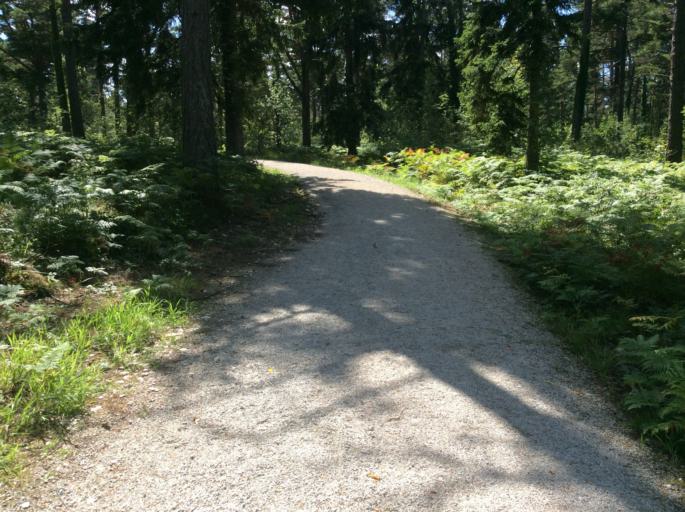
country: SE
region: Gotland
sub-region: Gotland
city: Vibble
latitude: 57.6028
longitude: 18.2769
